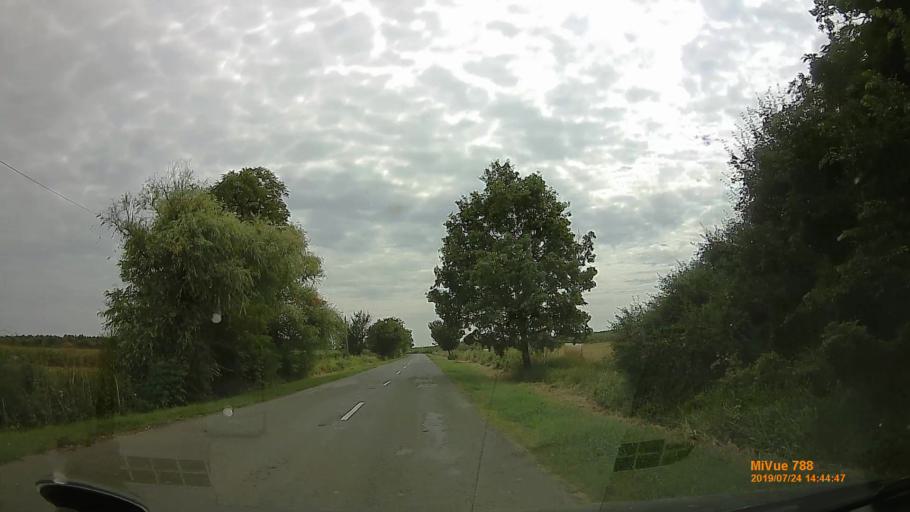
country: HU
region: Szabolcs-Szatmar-Bereg
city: Mandok
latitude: 48.2997
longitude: 22.2848
